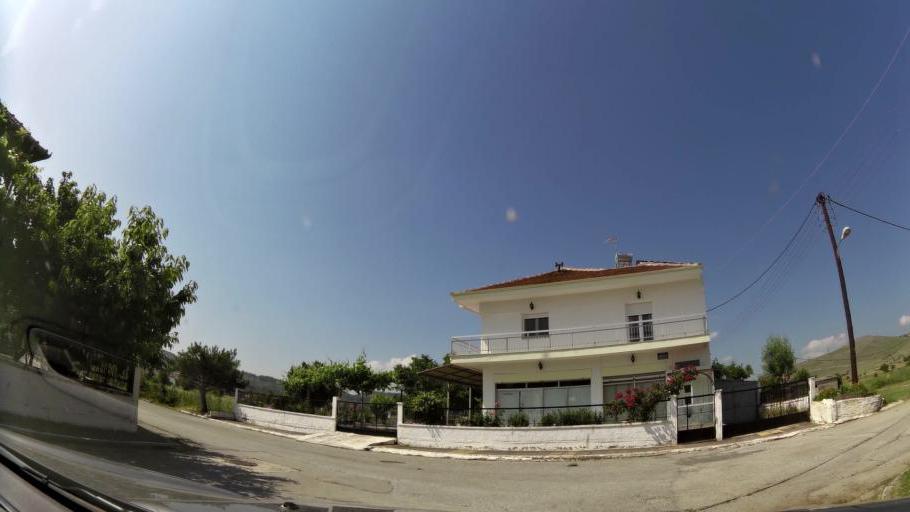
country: GR
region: West Macedonia
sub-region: Nomos Kozanis
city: Koila
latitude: 40.3364
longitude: 21.7870
